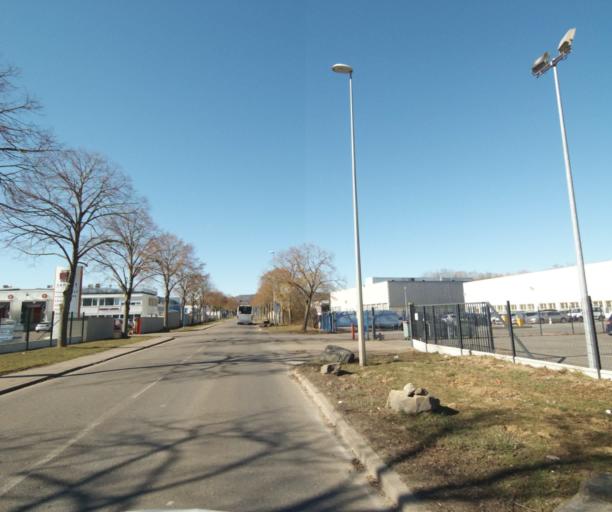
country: FR
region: Lorraine
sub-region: Departement de Meurthe-et-Moselle
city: Fleville-devant-Nancy
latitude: 48.6154
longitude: 6.1872
